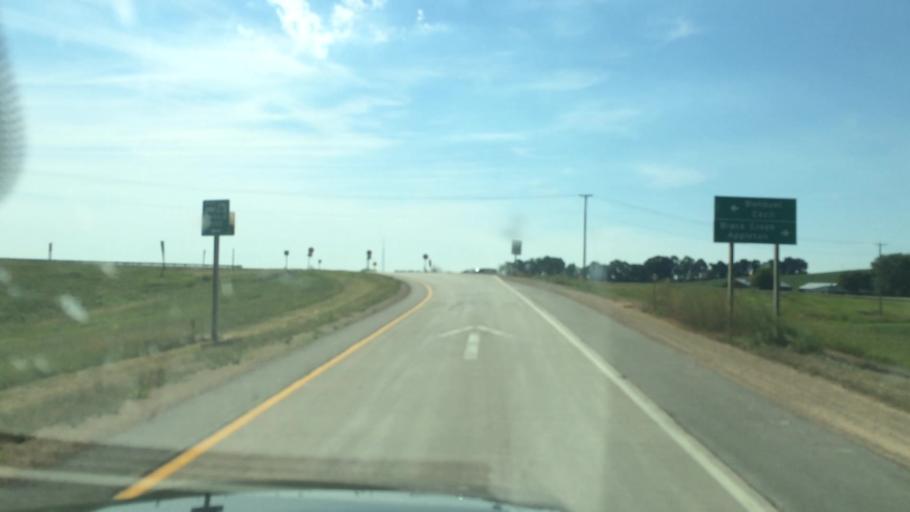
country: US
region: Wisconsin
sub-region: Shawano County
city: Bonduel
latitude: 44.7268
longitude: -88.4475
